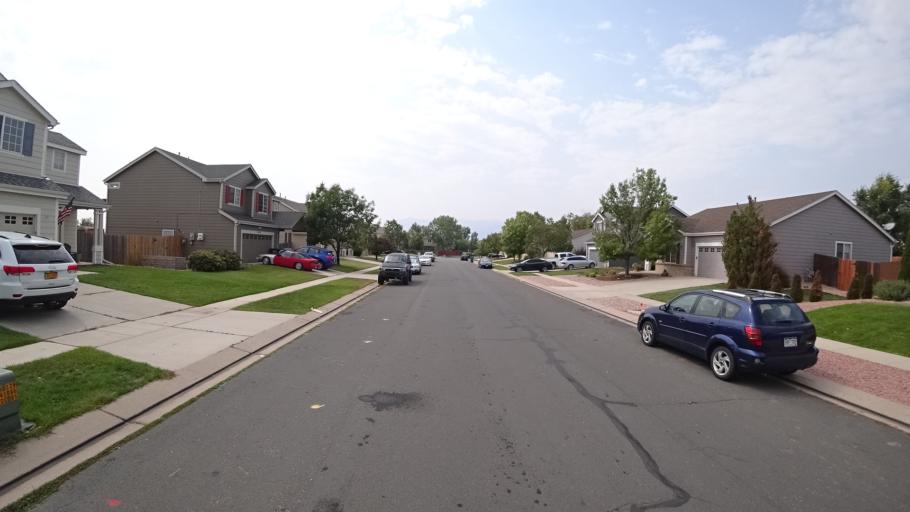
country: US
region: Colorado
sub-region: El Paso County
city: Cimarron Hills
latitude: 38.8224
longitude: -104.7324
